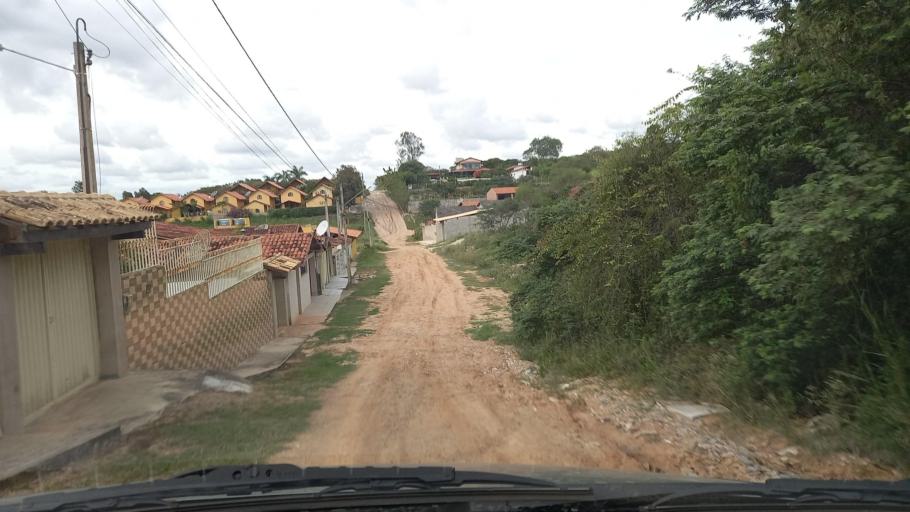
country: BR
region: Pernambuco
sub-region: Gravata
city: Gravata
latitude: -8.2042
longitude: -35.5453
